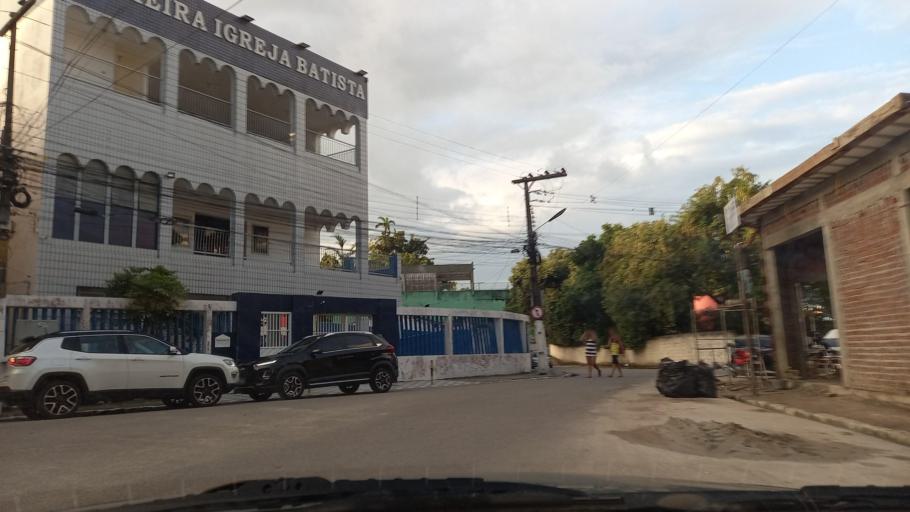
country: BR
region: Pernambuco
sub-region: Palmares
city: Palmares
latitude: -8.6826
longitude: -35.5867
